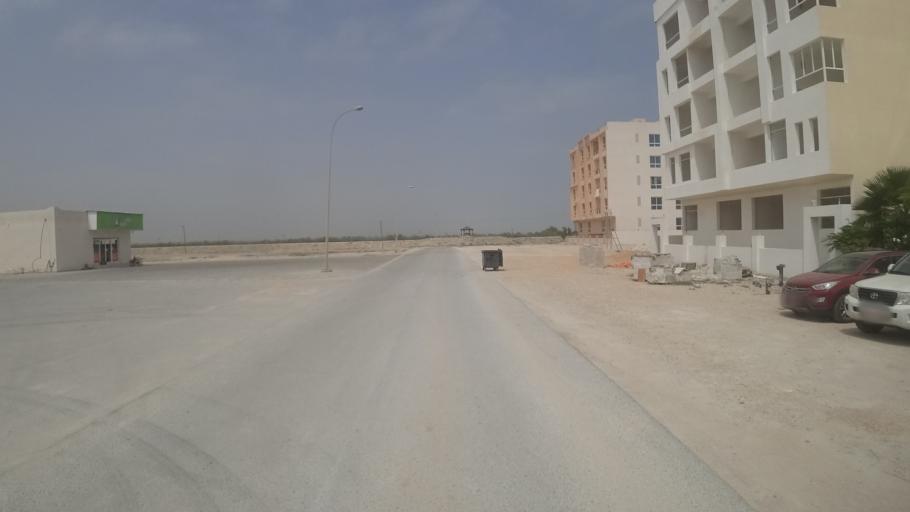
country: OM
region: Zufar
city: Salalah
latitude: 17.0142
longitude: 54.1737
